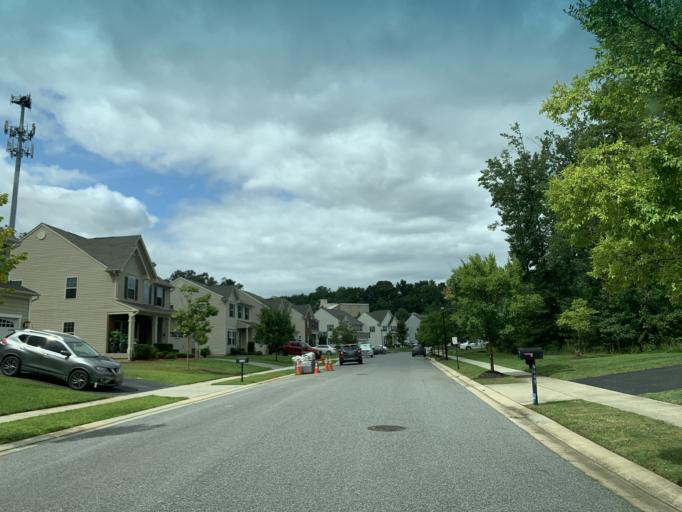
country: US
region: Maryland
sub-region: Baltimore County
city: White Marsh
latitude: 39.3901
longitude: -76.4208
